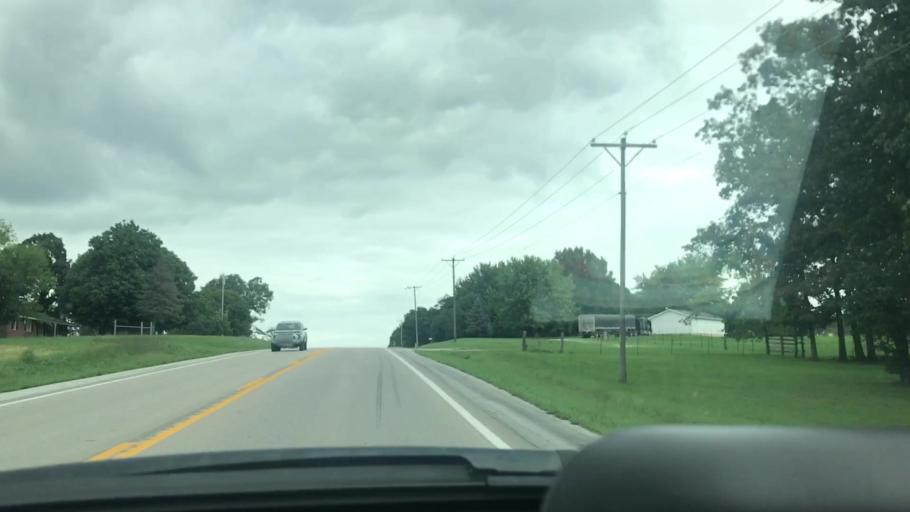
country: US
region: Missouri
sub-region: Dallas County
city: Buffalo
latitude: 37.6727
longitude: -93.1033
